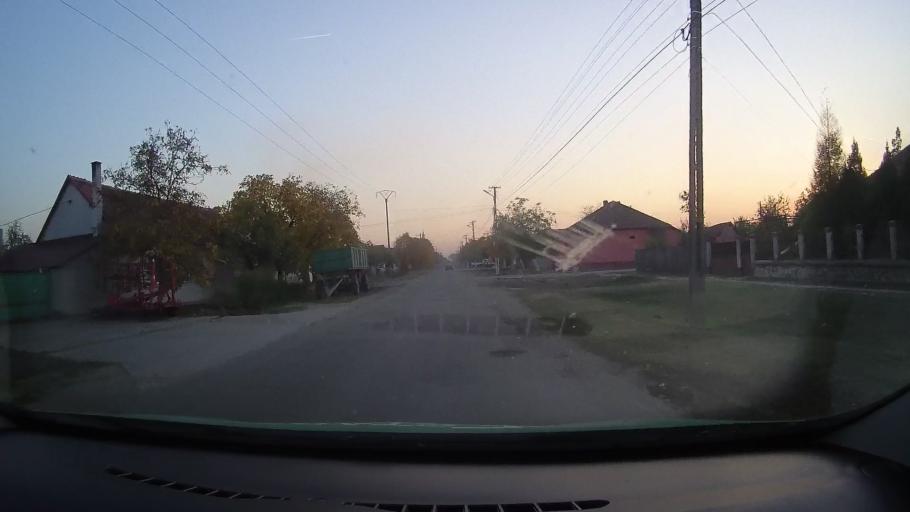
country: RO
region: Arad
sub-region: Comuna Olari
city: Olari
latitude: 46.3881
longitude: 21.5496
